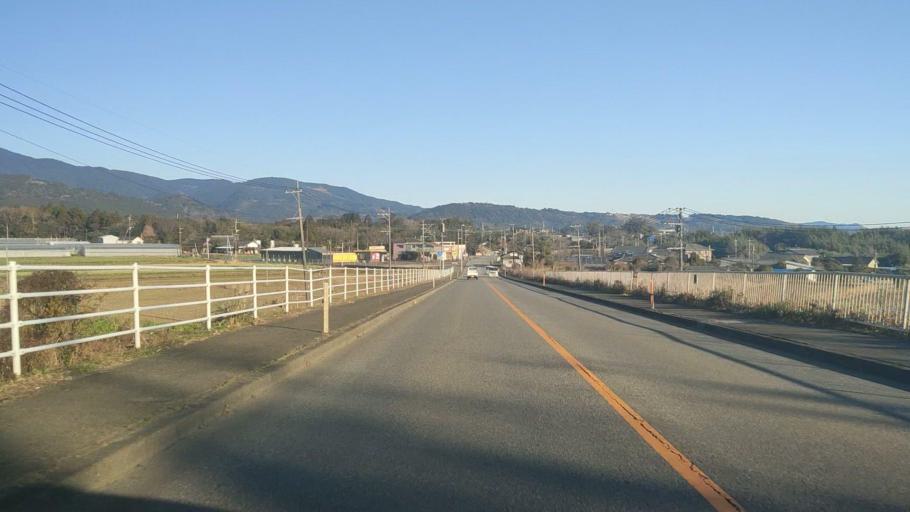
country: JP
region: Miyazaki
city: Takanabe
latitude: 32.2363
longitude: 131.5485
